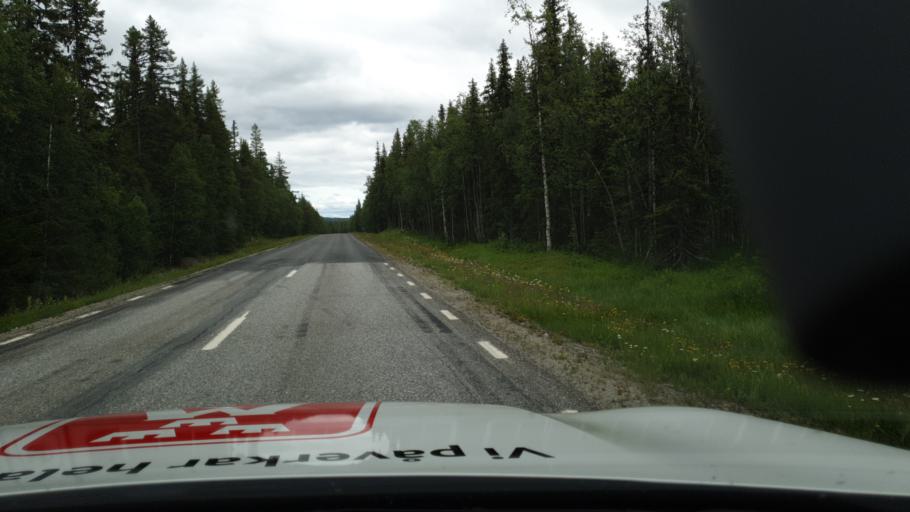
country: SE
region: Vaesterbotten
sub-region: Lycksele Kommun
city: Soderfors
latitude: 64.6396
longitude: 17.8823
